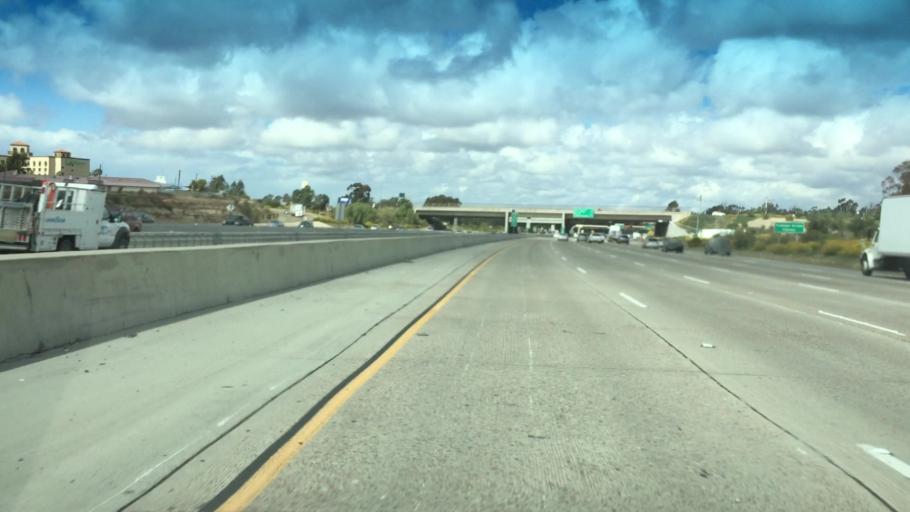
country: US
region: California
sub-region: San Diego County
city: Poway
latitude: 32.8900
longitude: -117.1137
